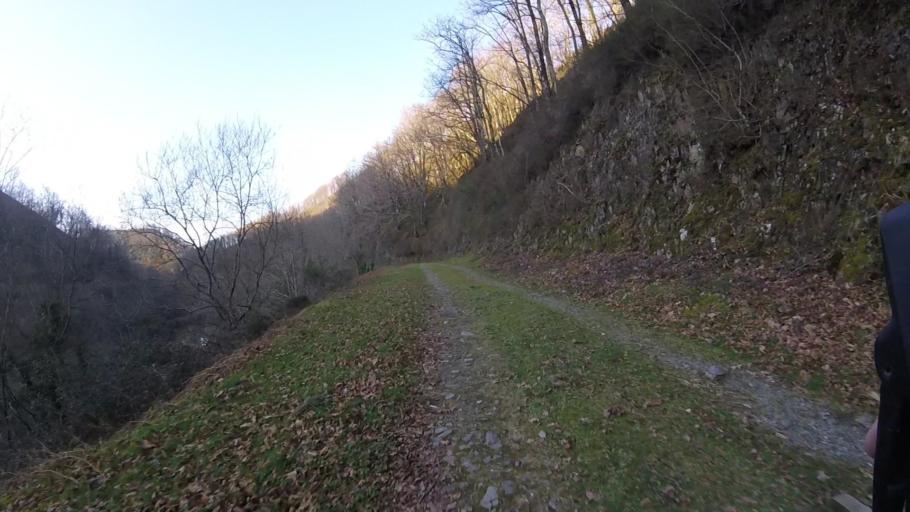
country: ES
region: Navarre
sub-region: Provincia de Navarra
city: Arano
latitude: 43.2138
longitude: -1.8624
